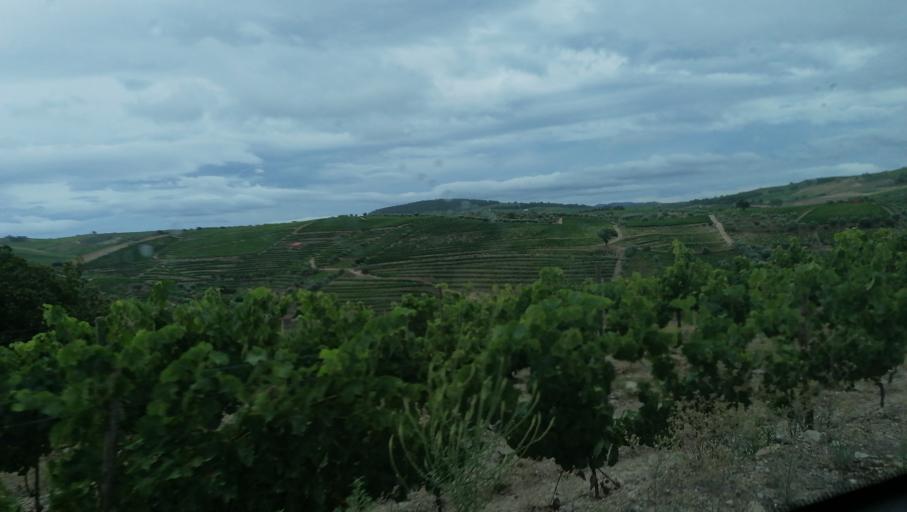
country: PT
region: Vila Real
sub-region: Sabrosa
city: Sabrosa
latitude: 41.2416
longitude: -7.4965
